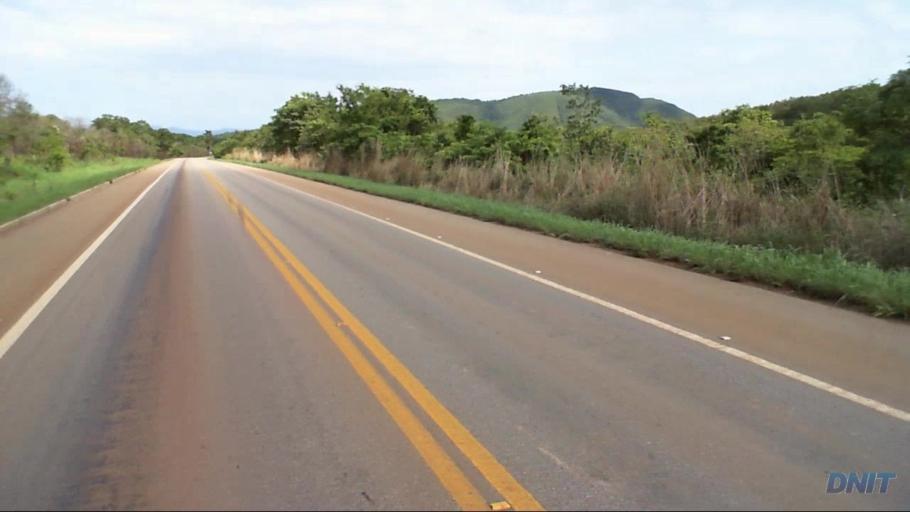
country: BR
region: Goias
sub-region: Barro Alto
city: Barro Alto
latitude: -15.1562
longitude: -48.8033
